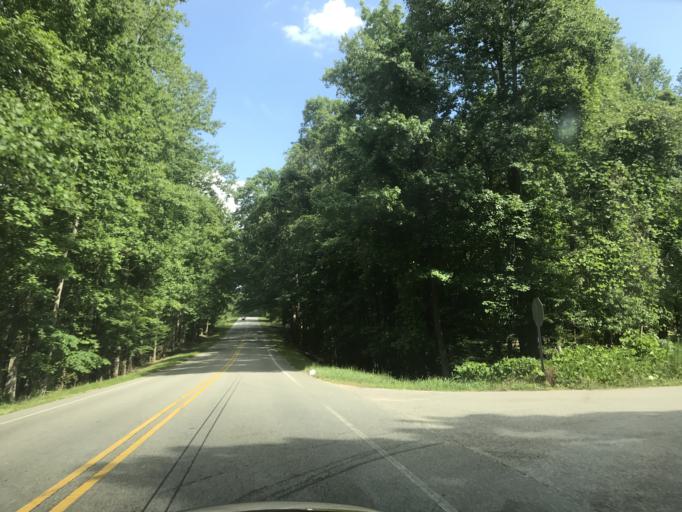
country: US
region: North Carolina
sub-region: Nash County
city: Spring Hope
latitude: 35.9256
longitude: -78.1916
